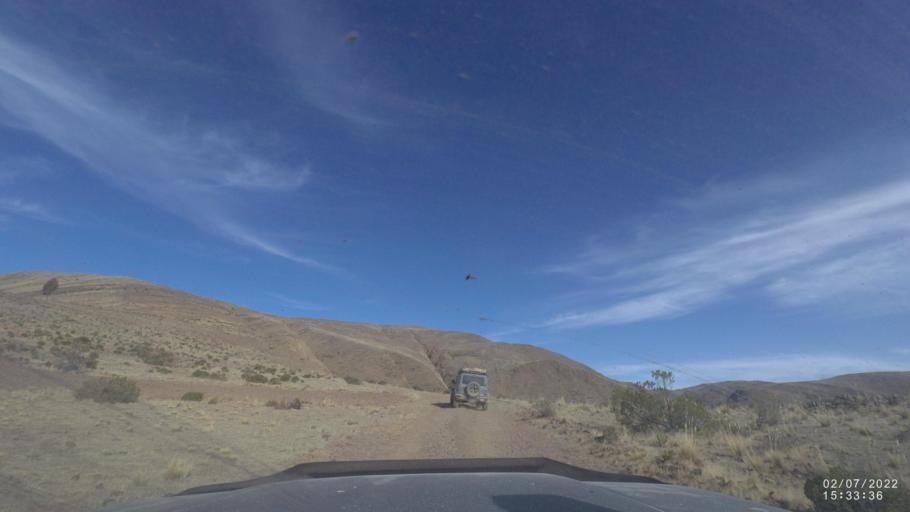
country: BO
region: Cochabamba
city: Irpa Irpa
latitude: -17.8866
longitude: -66.4140
